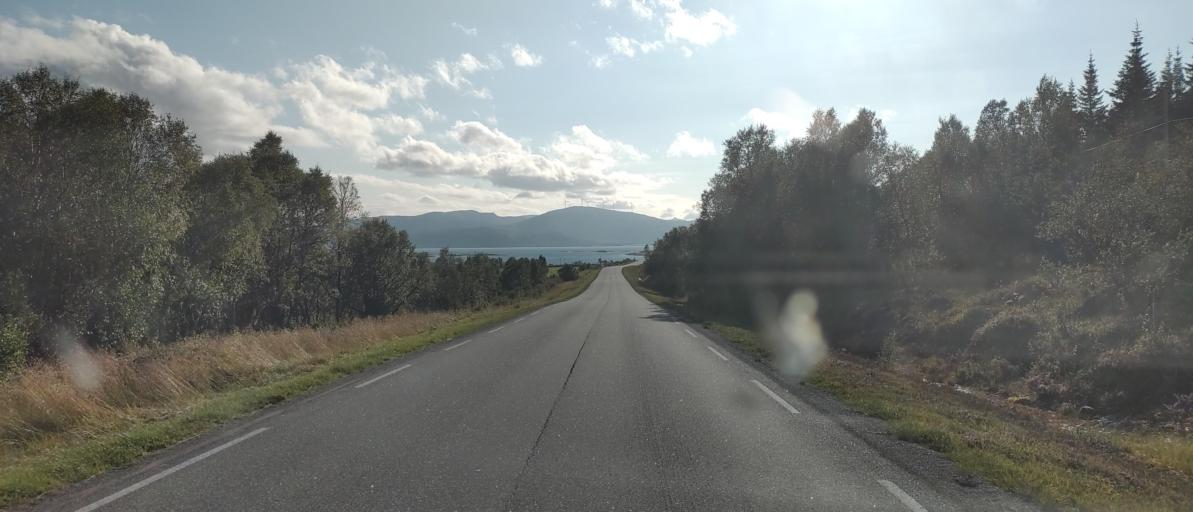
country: NO
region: Nordland
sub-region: Sortland
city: Sortland
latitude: 68.7910
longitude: 15.5031
